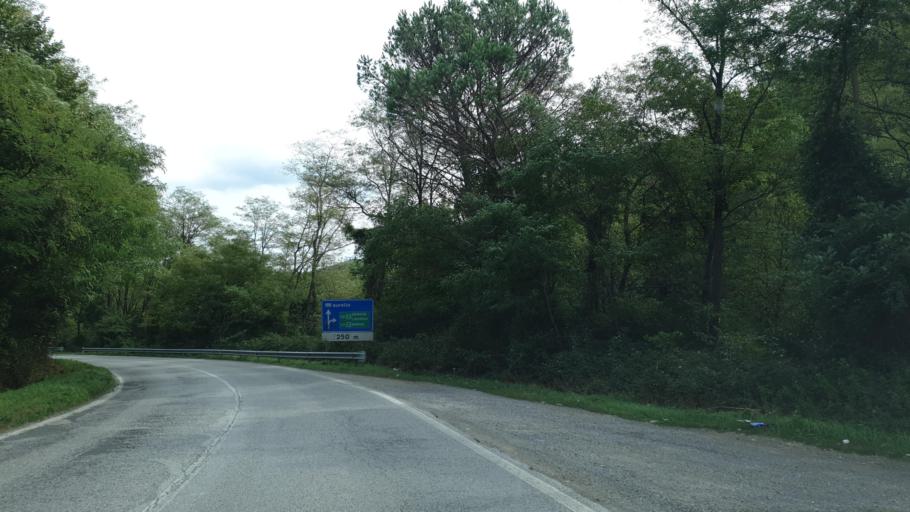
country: IT
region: Liguria
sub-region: Provincia di La Spezia
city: Carrodano
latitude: 44.2372
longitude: 9.6446
